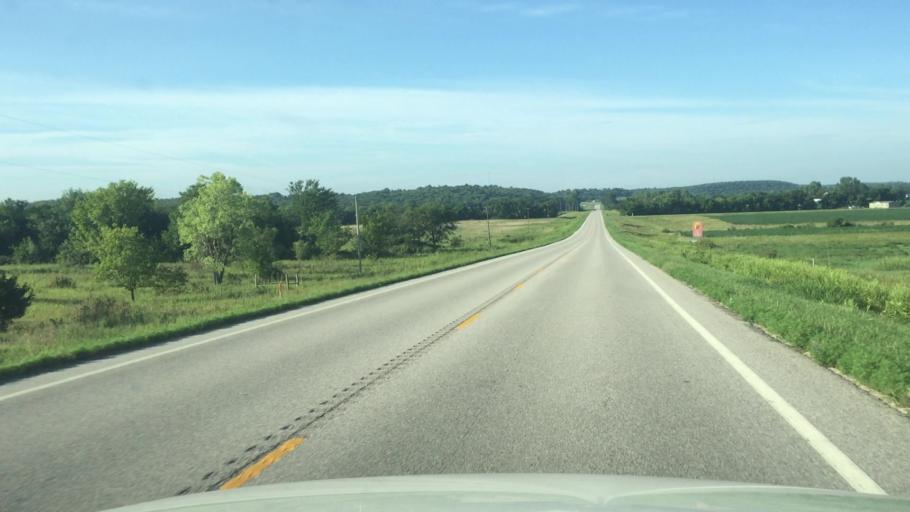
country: US
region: Kansas
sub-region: Anderson County
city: Garnett
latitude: 38.3805
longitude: -95.1124
